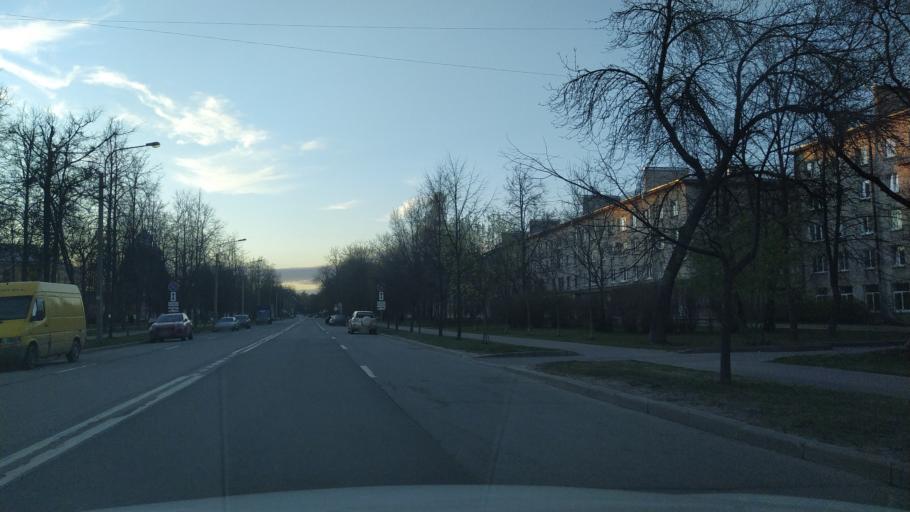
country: RU
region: St.-Petersburg
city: Pushkin
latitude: 59.7048
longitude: 30.4063
